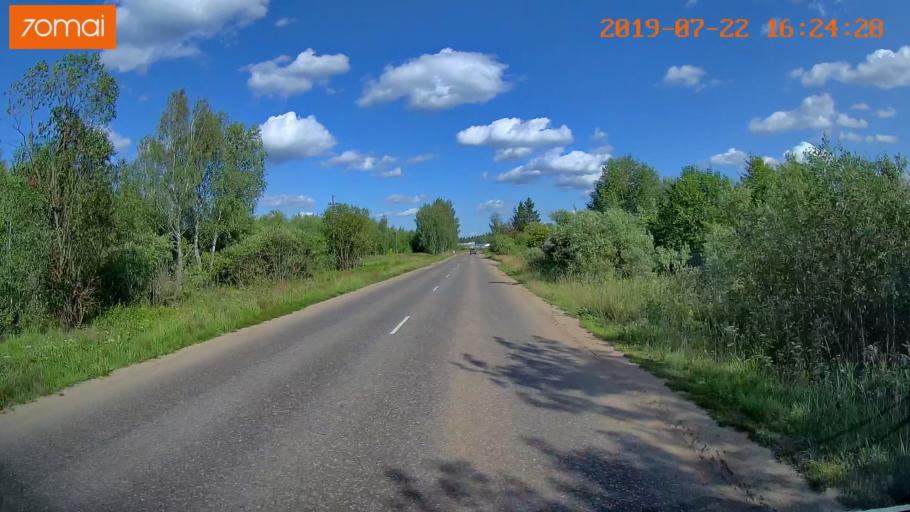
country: RU
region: Ivanovo
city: Novo-Talitsy
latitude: 57.0581
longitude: 40.9140
